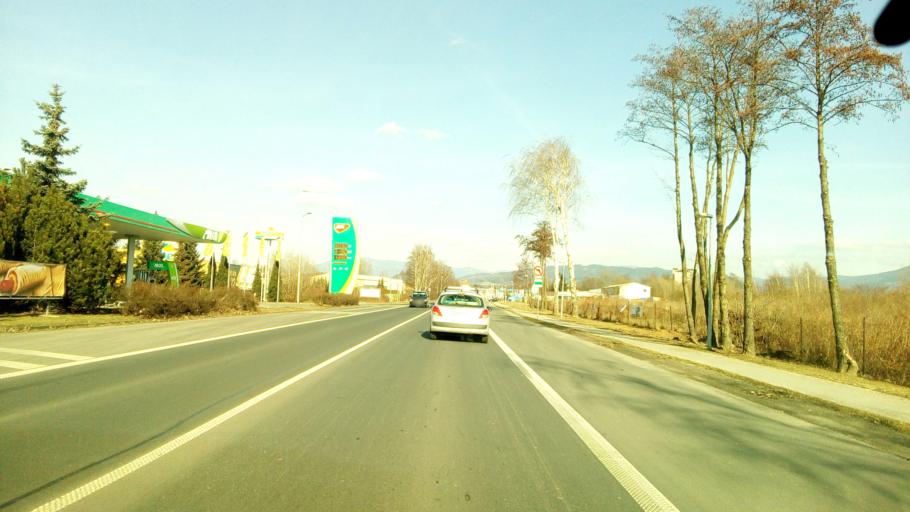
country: CZ
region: Olomoucky
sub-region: Okres Sumperk
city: Sumperk
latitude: 49.9559
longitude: 16.9683
